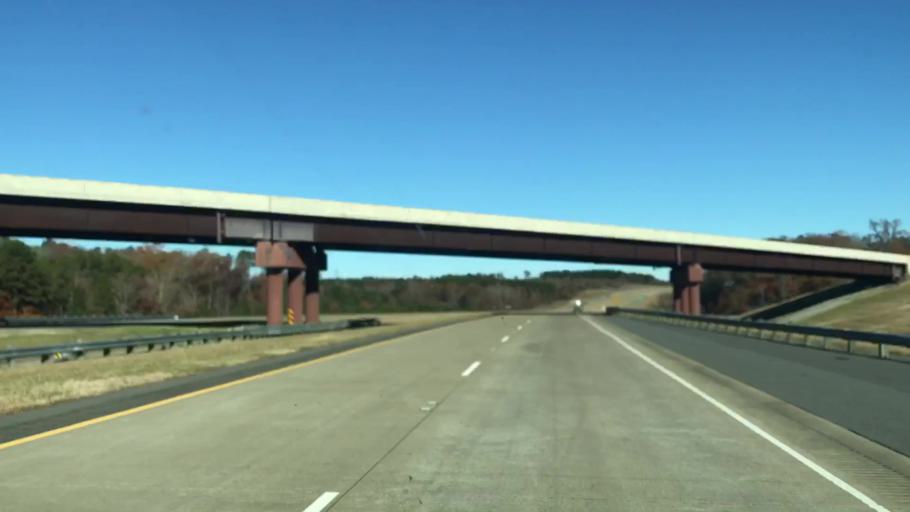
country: US
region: Louisiana
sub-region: Caddo Parish
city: Vivian
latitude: 32.9780
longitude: -93.9095
